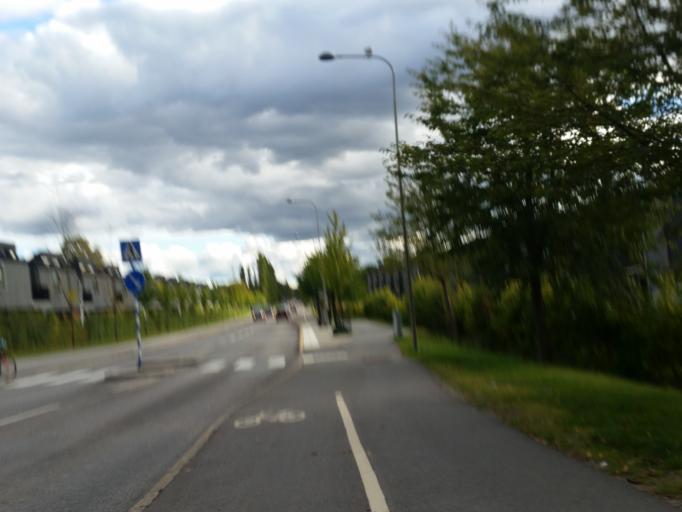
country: SE
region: Stockholm
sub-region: Nacka Kommun
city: Nacka
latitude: 59.2712
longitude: 18.1115
